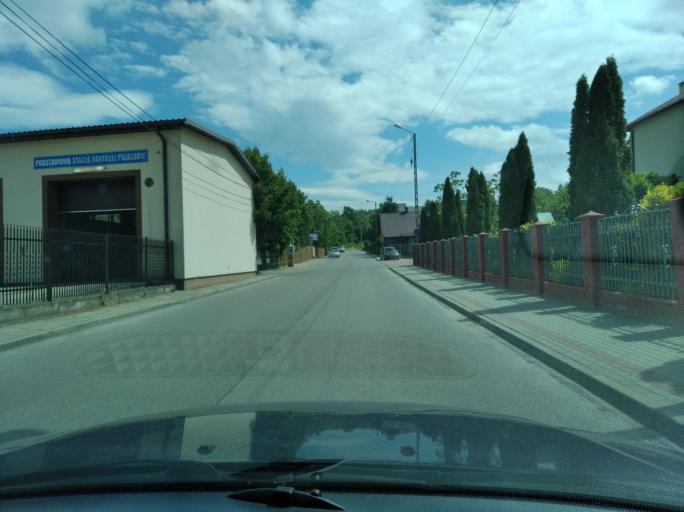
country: PL
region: Subcarpathian Voivodeship
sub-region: Powiat ropczycko-sedziszowski
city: Ropczyce
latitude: 50.0520
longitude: 21.6155
